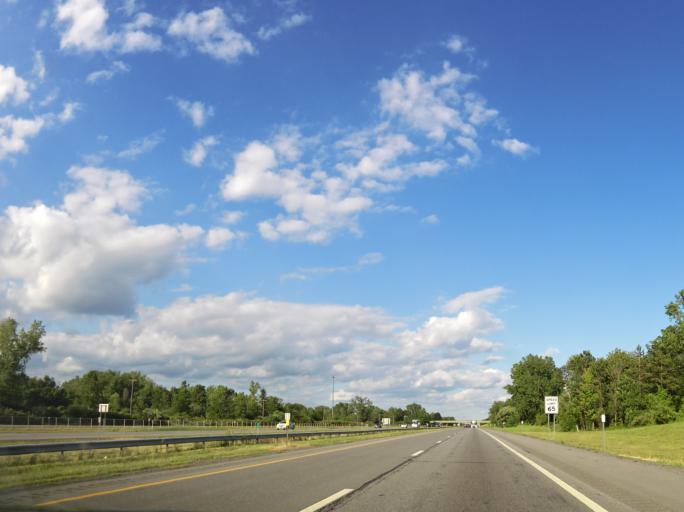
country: US
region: New York
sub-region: Erie County
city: Clarence
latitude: 42.9525
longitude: -78.6000
